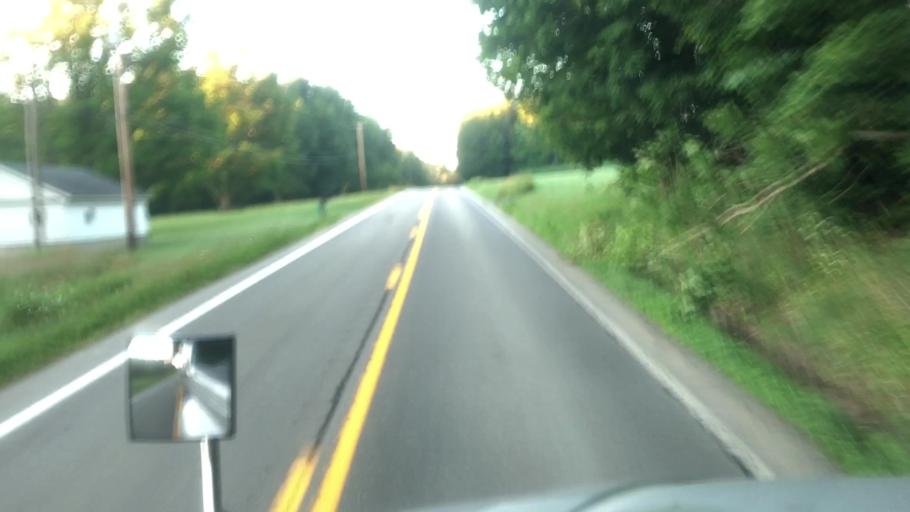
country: US
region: Pennsylvania
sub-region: Crawford County
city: Titusville
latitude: 41.5823
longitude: -79.6098
